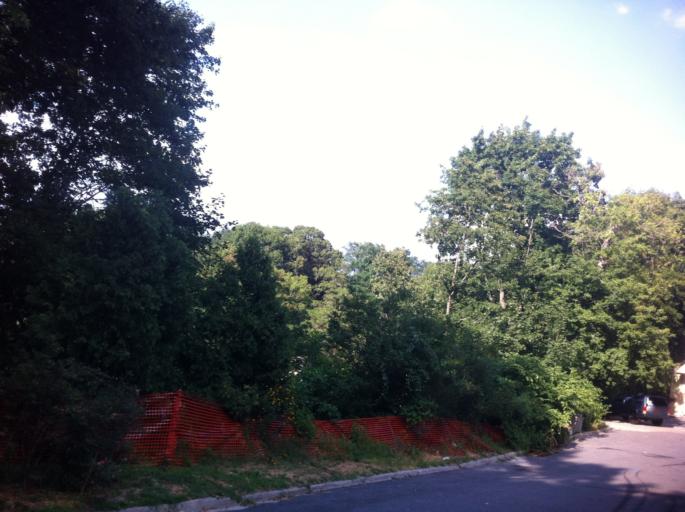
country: US
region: New York
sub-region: Nassau County
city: Sea Cliff
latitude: 40.8504
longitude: -73.6421
